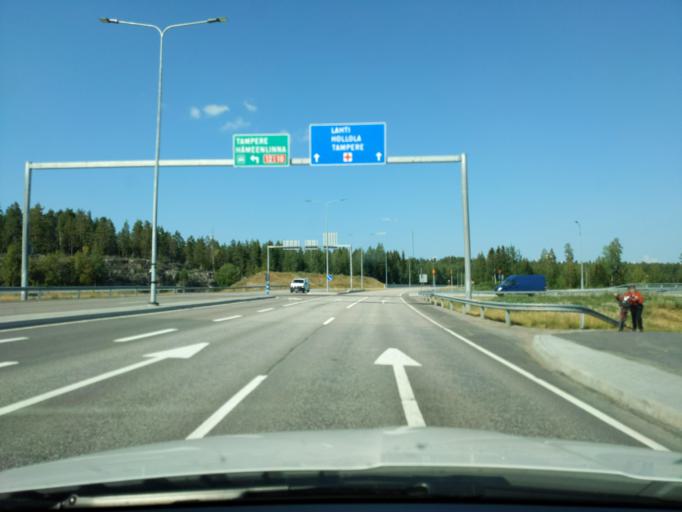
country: FI
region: Paijanne Tavastia
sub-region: Lahti
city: Hollola
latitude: 60.9805
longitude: 25.4860
